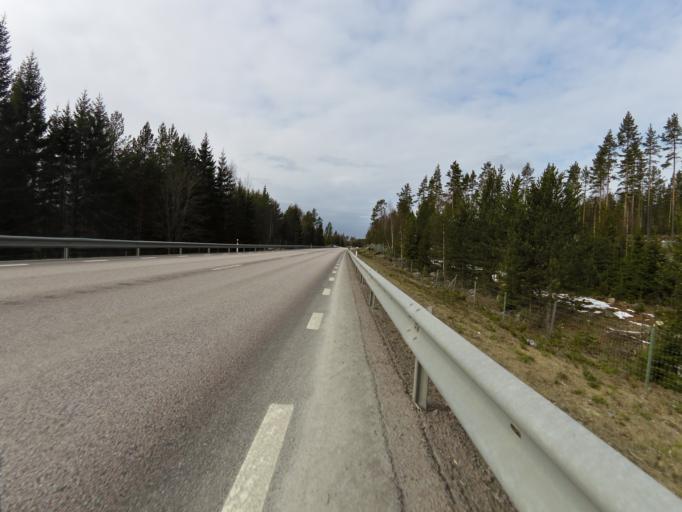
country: SE
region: Gaevleborg
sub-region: Hofors Kommun
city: Hofors
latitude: 60.5451
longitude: 16.1446
